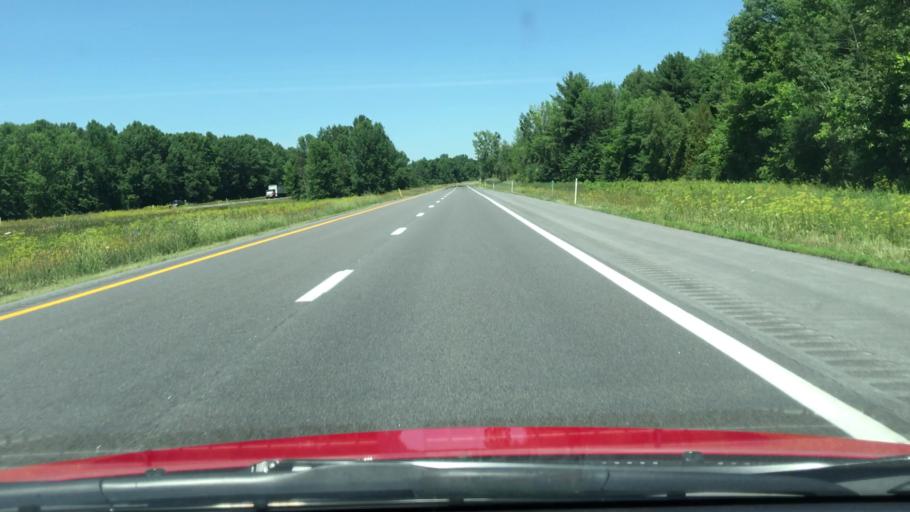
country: US
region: New York
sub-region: Clinton County
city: Cumberland Head
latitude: 44.8474
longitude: -73.4475
